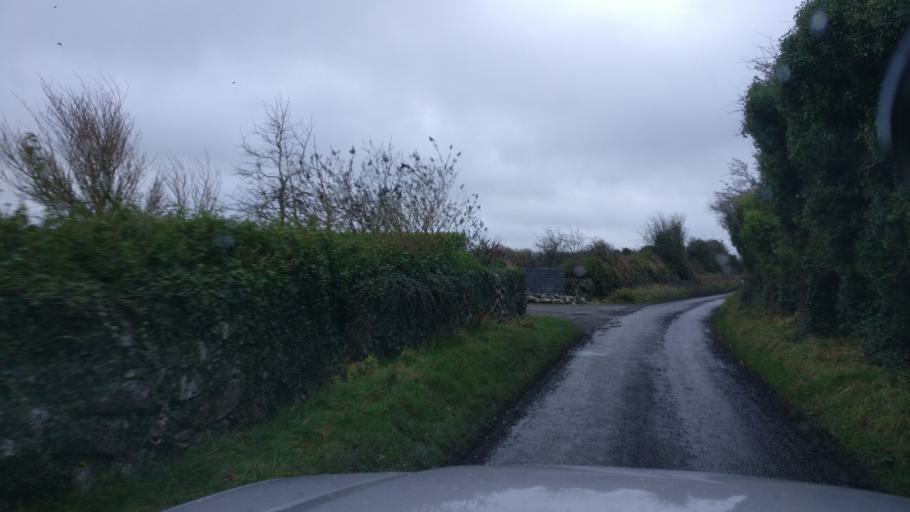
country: IE
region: Connaught
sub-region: County Galway
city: Loughrea
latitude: 53.2025
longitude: -8.6708
